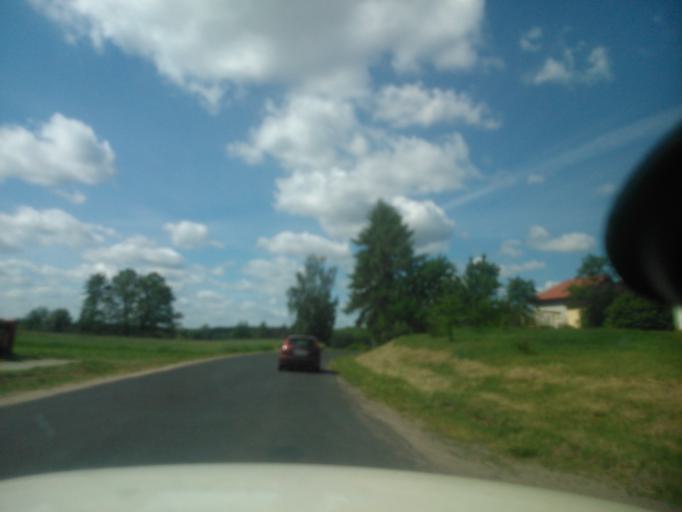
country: PL
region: Kujawsko-Pomorskie
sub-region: Powiat golubsko-dobrzynski
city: Golub-Dobrzyn
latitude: 53.0965
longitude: 19.0107
